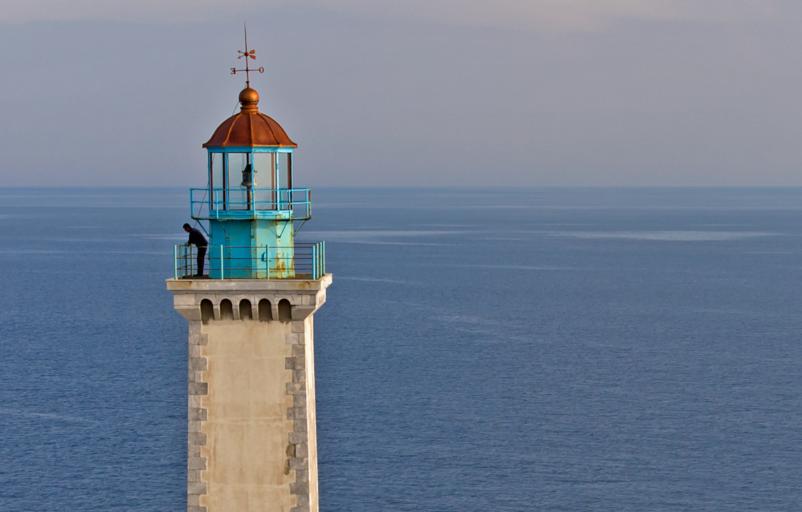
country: GR
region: Peloponnese
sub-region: Nomos Lakonias
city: Gytheio
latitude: 36.3866
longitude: 22.4828
